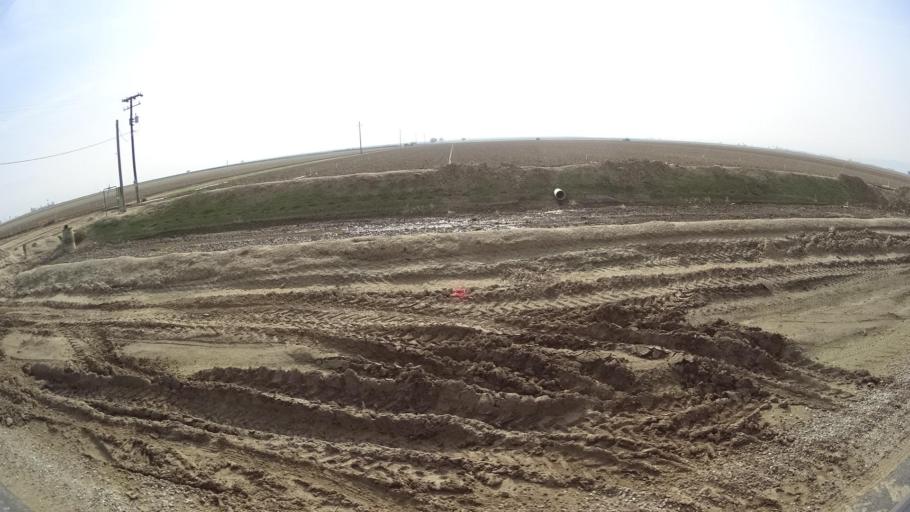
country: US
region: California
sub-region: Kern County
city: Arvin
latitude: 35.0455
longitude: -118.8913
